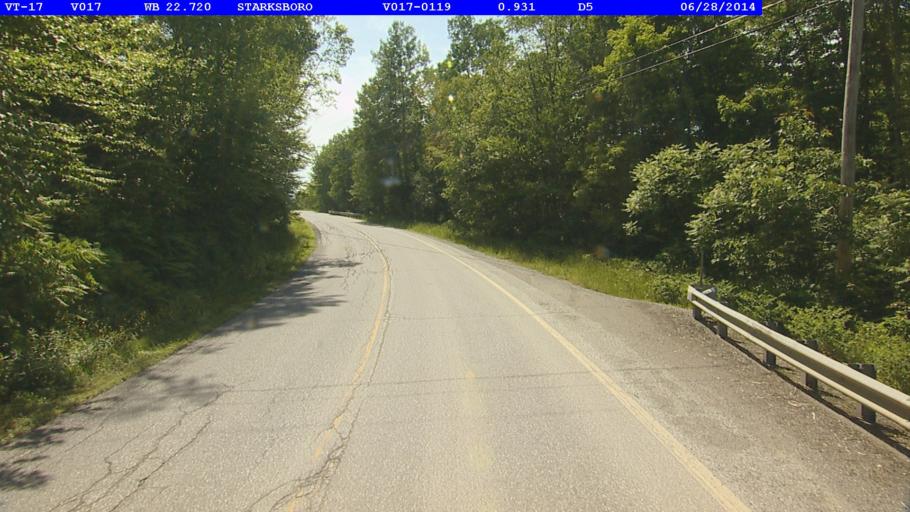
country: US
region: Vermont
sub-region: Addison County
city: Bristol
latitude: 44.1694
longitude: -73.0026
